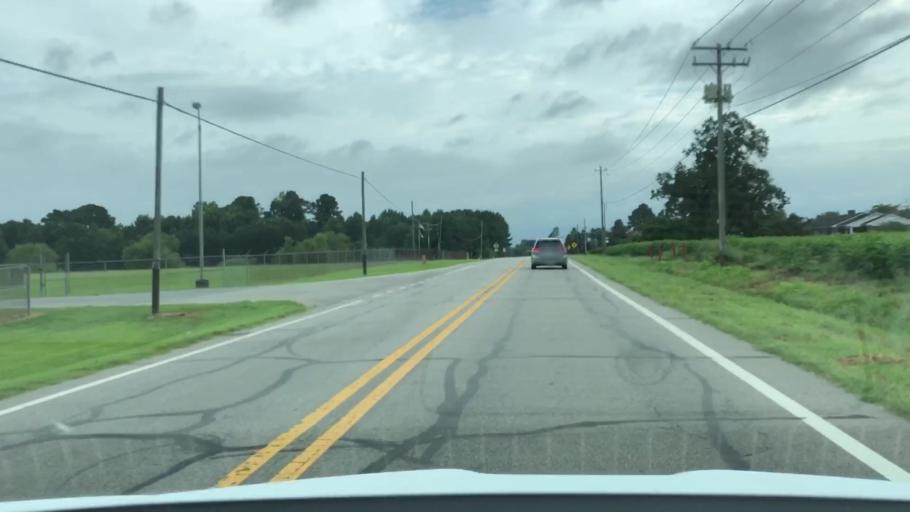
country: US
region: North Carolina
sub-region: Lenoir County
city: Kinston
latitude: 35.2283
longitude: -77.5753
